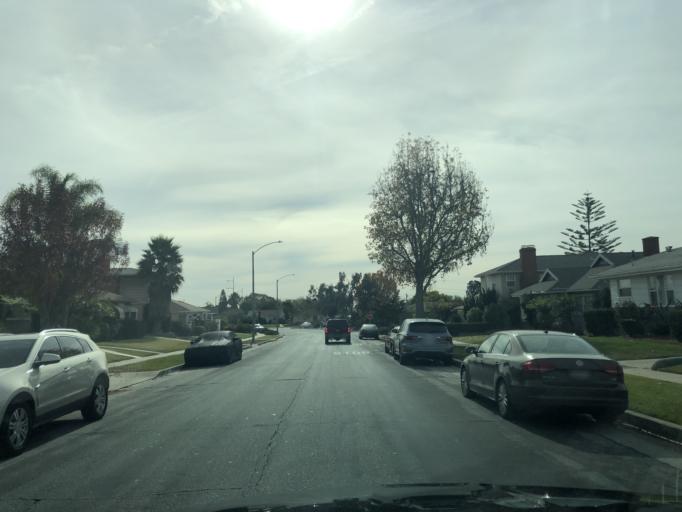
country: US
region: California
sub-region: Los Angeles County
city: Ladera Heights
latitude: 33.9829
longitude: -118.3613
